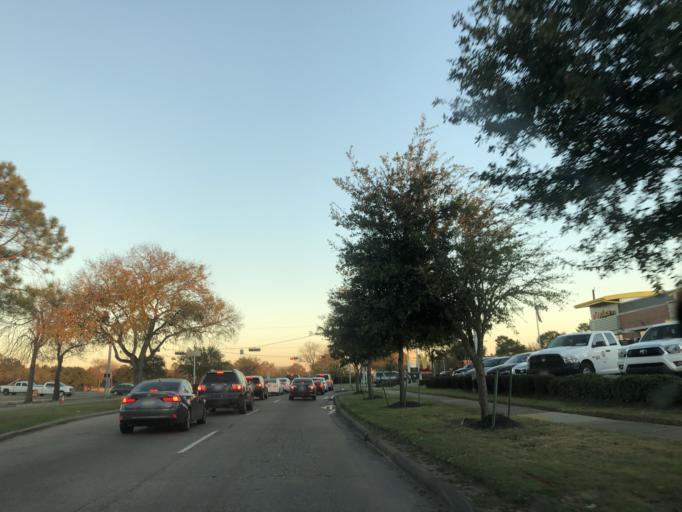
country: US
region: Texas
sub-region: Harris County
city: Bellaire
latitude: 29.6778
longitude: -95.4944
